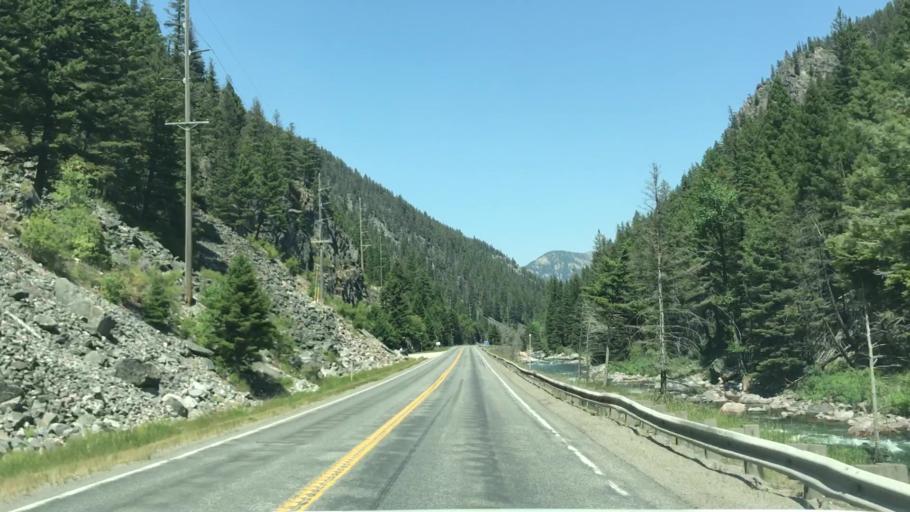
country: US
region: Montana
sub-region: Gallatin County
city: Big Sky
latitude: 45.4167
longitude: -111.2329
